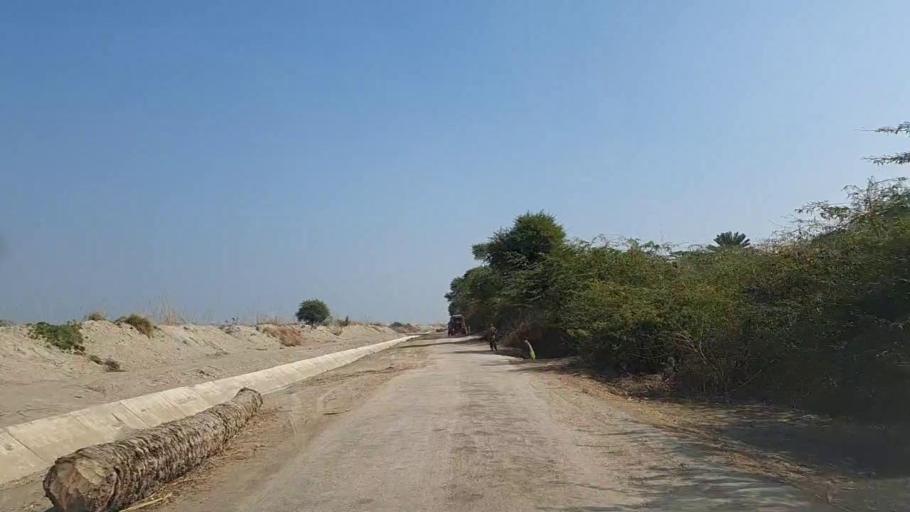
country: PK
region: Sindh
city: Jam Sahib
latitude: 26.2709
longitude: 68.5645
